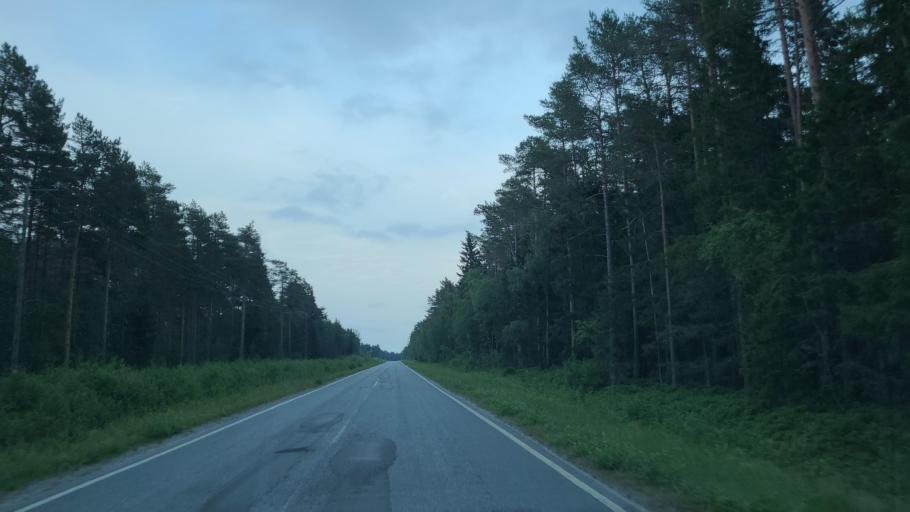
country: FI
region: Ostrobothnia
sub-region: Vaasa
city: Replot
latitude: 63.2031
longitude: 21.2795
